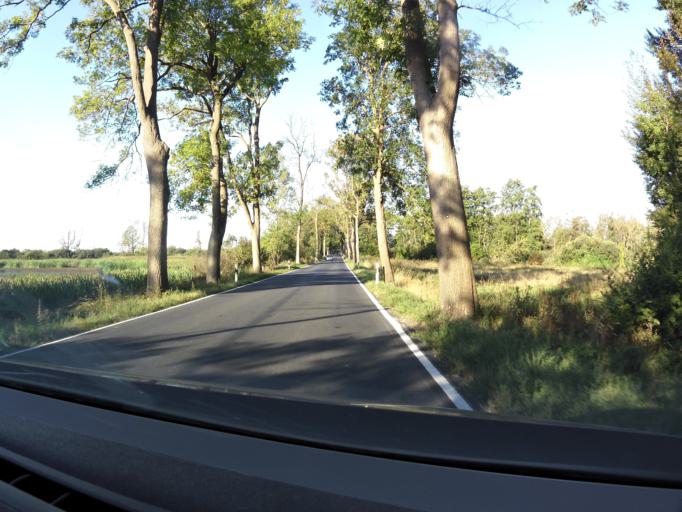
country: DE
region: Mecklenburg-Vorpommern
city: Alt-Sanitz
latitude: 53.8225
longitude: 13.5106
